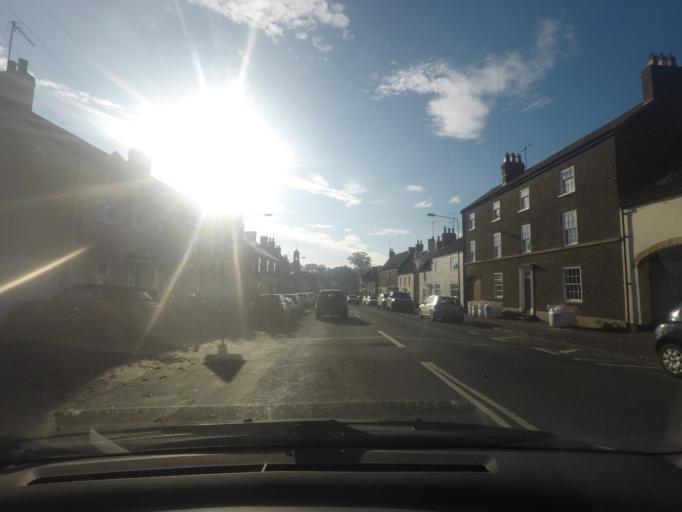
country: GB
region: England
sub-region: East Riding of Yorkshire
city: South Cave
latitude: 53.7706
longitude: -0.6010
